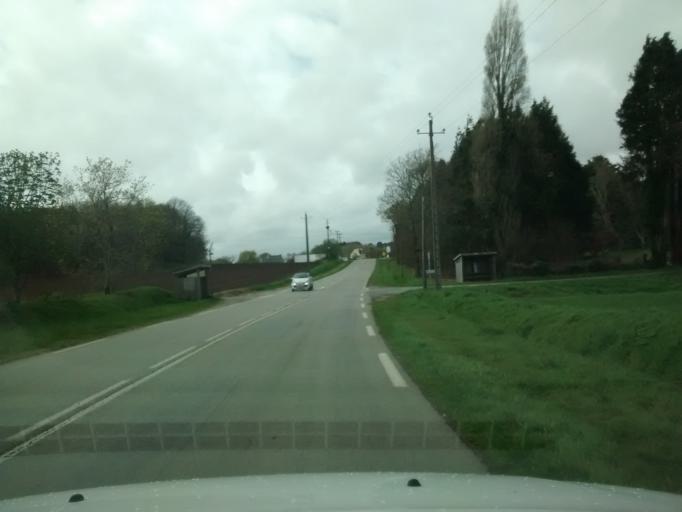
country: FR
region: Brittany
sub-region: Departement du Morbihan
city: Gestel
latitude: 47.7969
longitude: -3.4718
